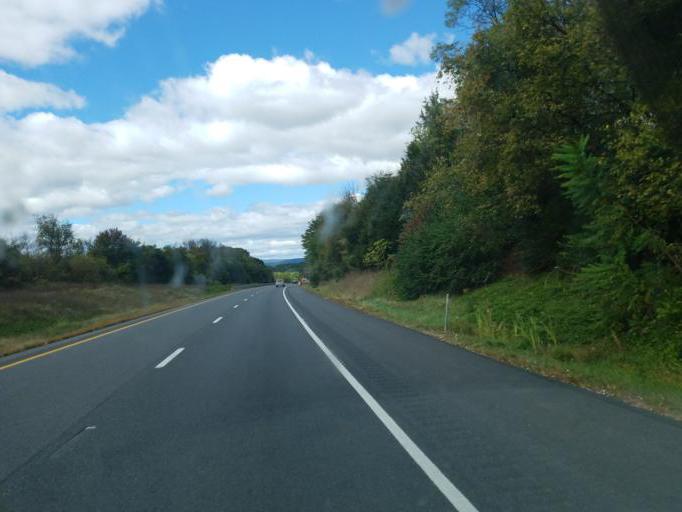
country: US
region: Maryland
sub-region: Washington County
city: Wilson-Conococheague
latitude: 39.6388
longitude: -77.8247
